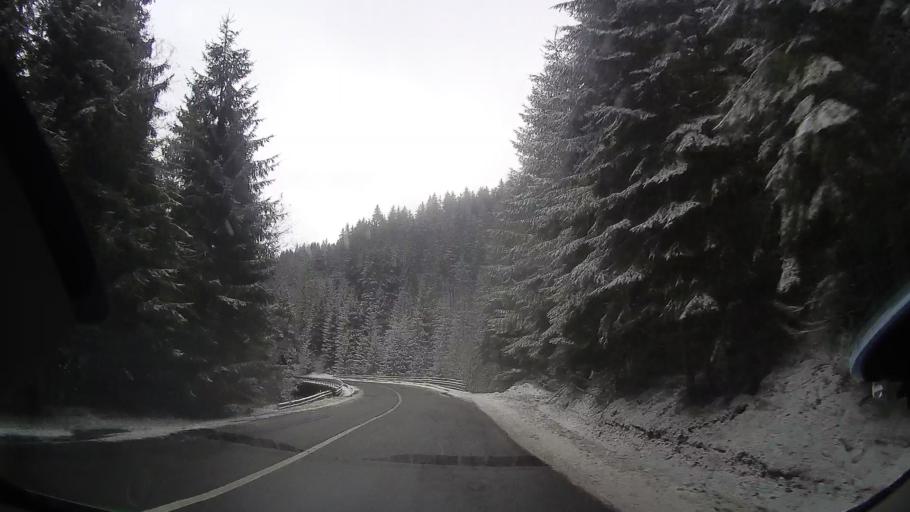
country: RO
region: Cluj
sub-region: Comuna Belis
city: Belis
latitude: 46.6564
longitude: 23.0545
